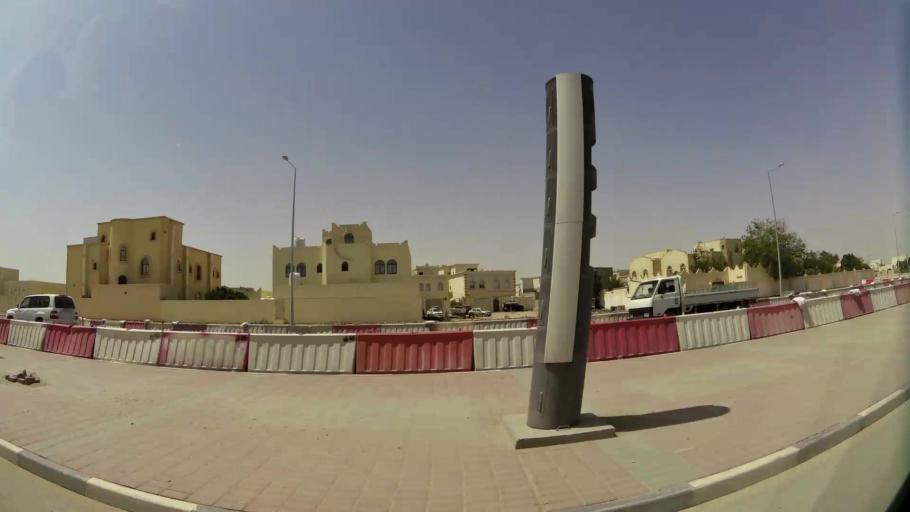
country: QA
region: Baladiyat Umm Salal
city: Umm Salal Muhammad
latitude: 25.3824
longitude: 51.4683
